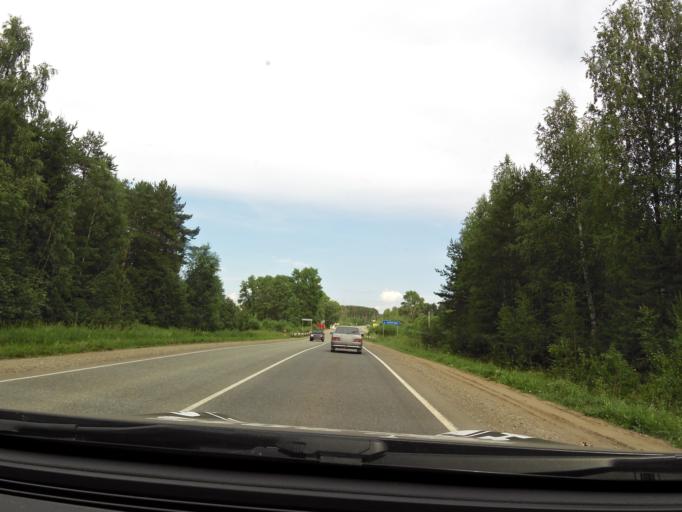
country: RU
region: Kirov
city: Vakhrushi
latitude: 58.6496
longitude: 49.8725
